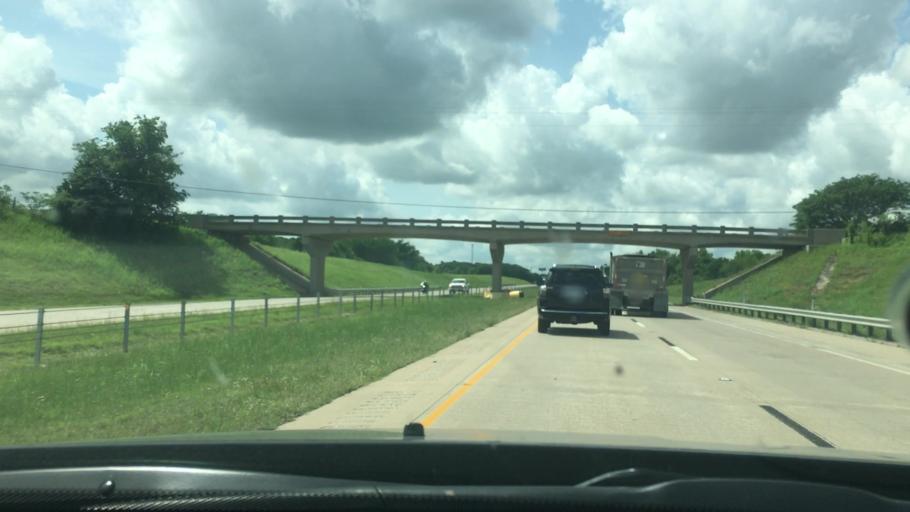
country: US
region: Oklahoma
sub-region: Love County
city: Marietta
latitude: 33.8541
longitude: -97.1343
